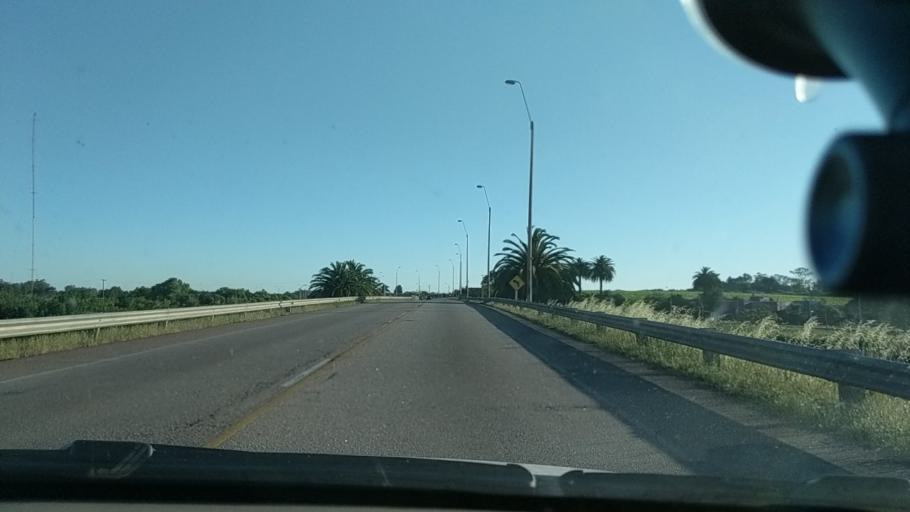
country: UY
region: Canelones
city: Canelones
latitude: -34.5421
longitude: -56.2741
